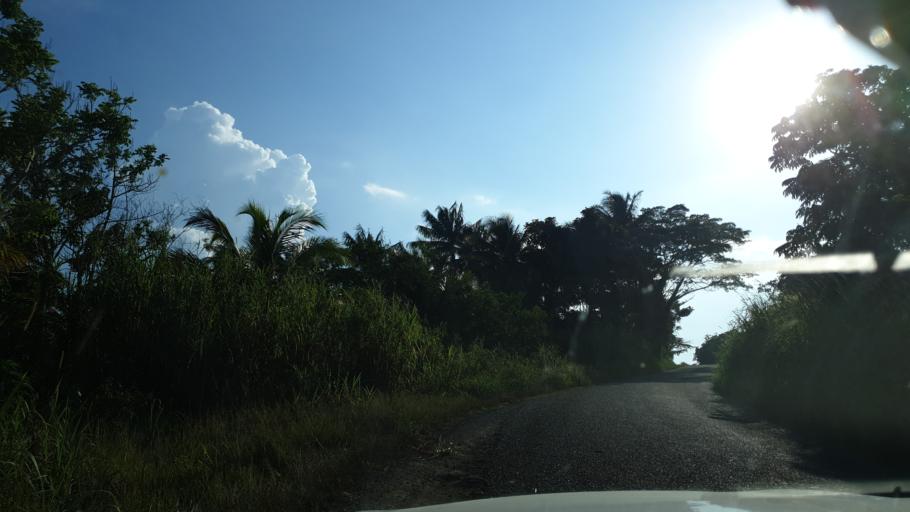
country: PG
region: East Sepik
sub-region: Wewak
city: Wewak
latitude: -3.6961
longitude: 143.6504
